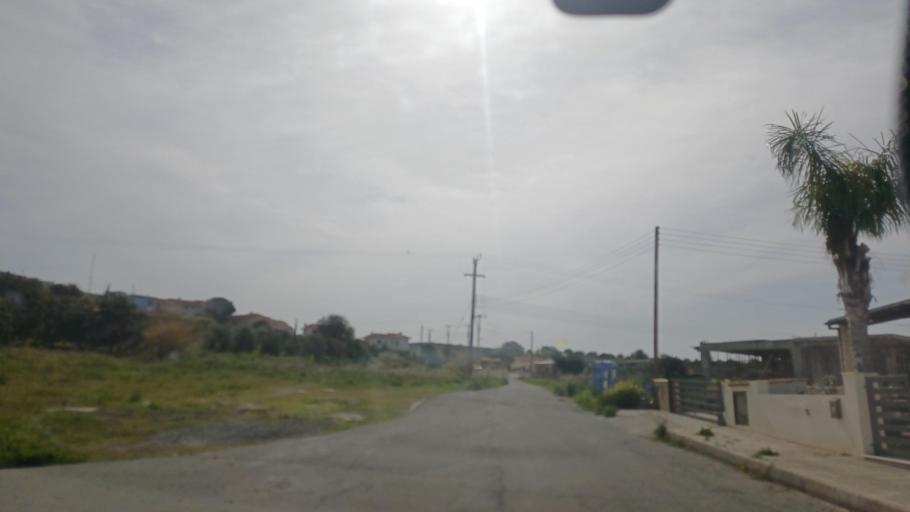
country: CY
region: Pafos
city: Mesogi
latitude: 34.7840
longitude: 32.4650
